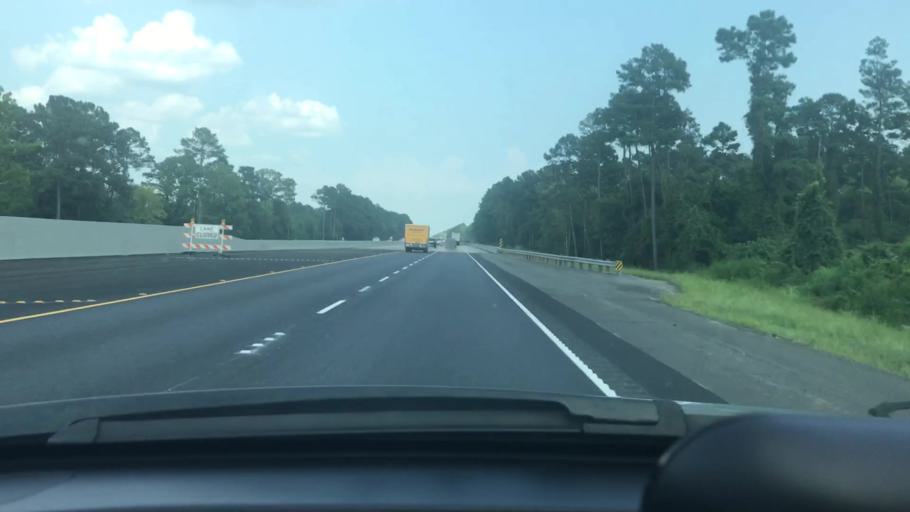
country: US
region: Louisiana
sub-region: Livingston Parish
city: Livingston
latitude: 30.4748
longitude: -90.6764
